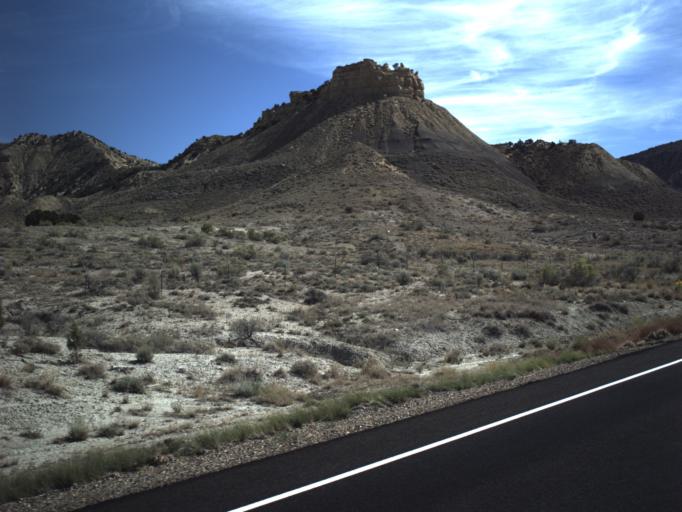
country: US
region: Utah
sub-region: Garfield County
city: Panguitch
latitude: 37.5960
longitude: -111.9456
